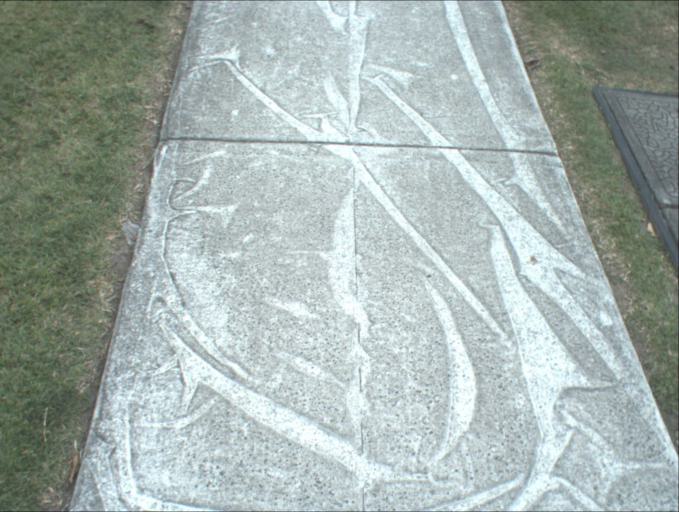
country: AU
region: Queensland
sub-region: Logan
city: Slacks Creek
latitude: -27.6794
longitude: 153.1773
